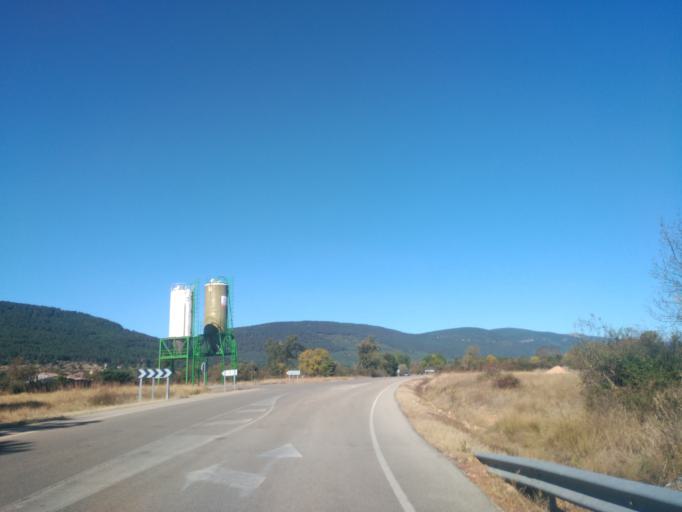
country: ES
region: Castille and Leon
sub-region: Provincia de Soria
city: Vinuesa
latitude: 41.9094
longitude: -2.7500
